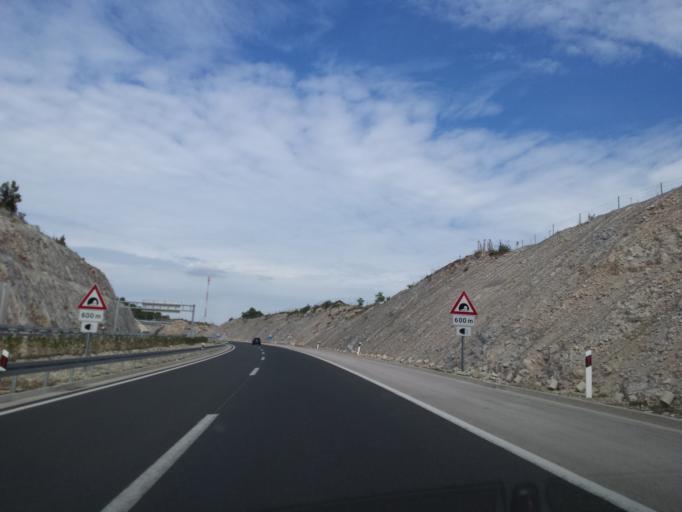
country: BA
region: Federation of Bosnia and Herzegovina
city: Ljubuski
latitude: 43.1581
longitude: 17.4779
